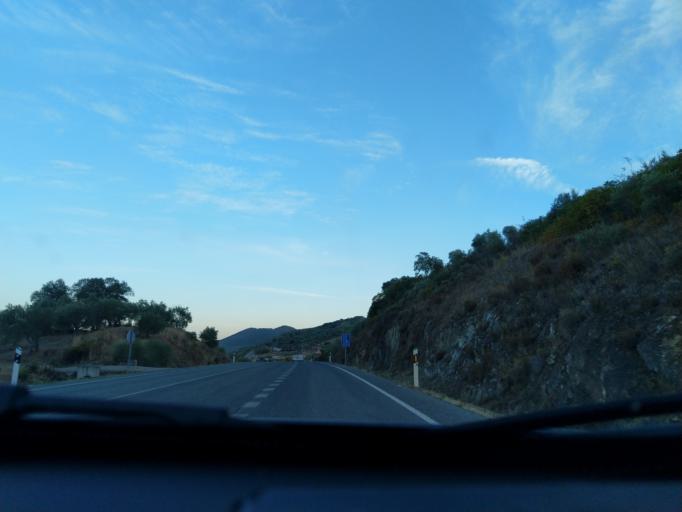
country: ES
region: Extremadura
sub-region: Provincia de Badajoz
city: Reina
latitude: 38.1552
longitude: -5.9052
